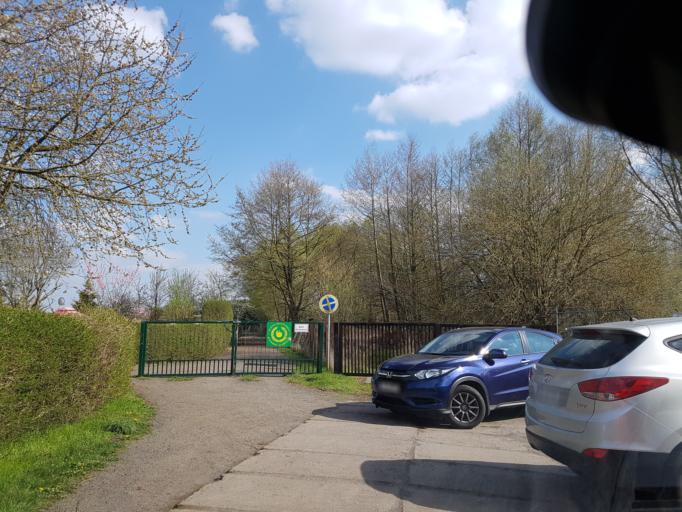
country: DE
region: Brandenburg
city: Juterbog
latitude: 51.9928
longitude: 13.0536
